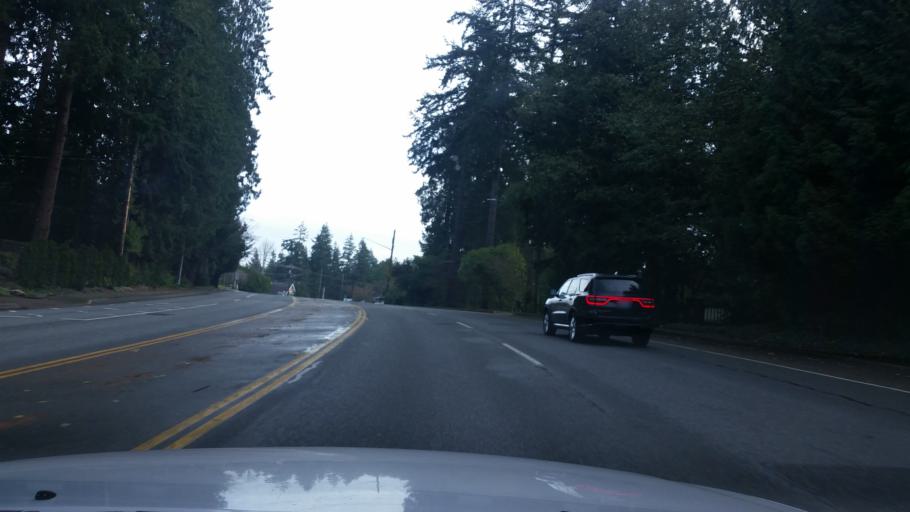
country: US
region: Washington
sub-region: Snohomish County
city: Woodway
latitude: 47.7960
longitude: -122.3758
